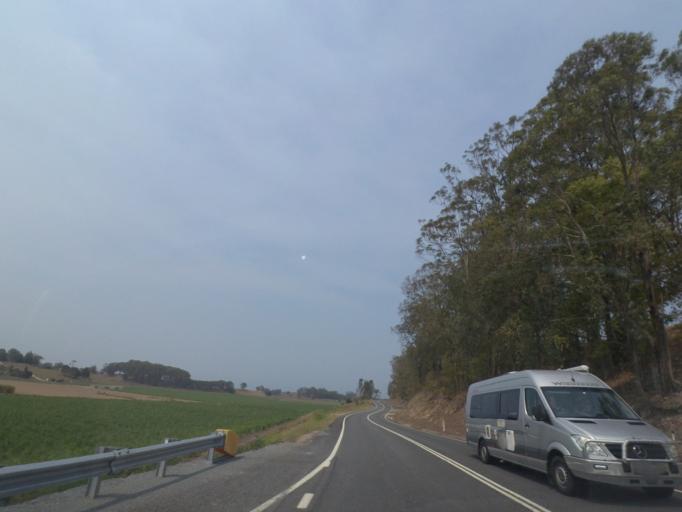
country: AU
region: New South Wales
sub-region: Tweed
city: Burringbar
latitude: -28.4587
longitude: 153.5187
